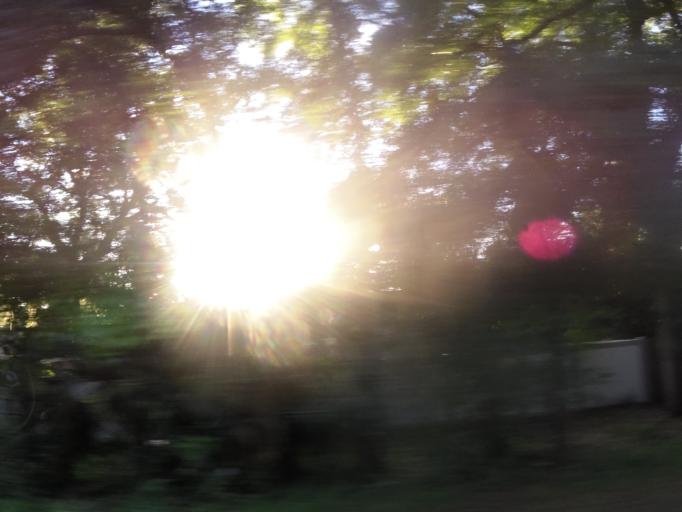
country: US
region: Florida
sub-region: Duval County
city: Atlantic Beach
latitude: 30.3747
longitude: -81.5123
